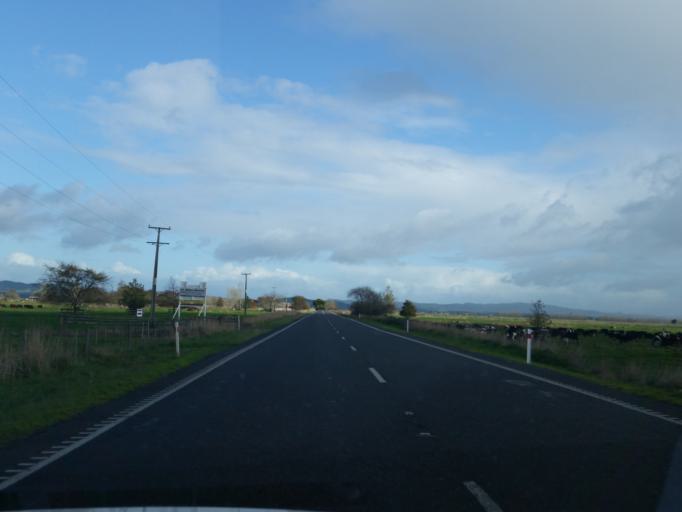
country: NZ
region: Waikato
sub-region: Hauraki District
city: Ngatea
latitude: -37.2761
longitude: 175.4722
